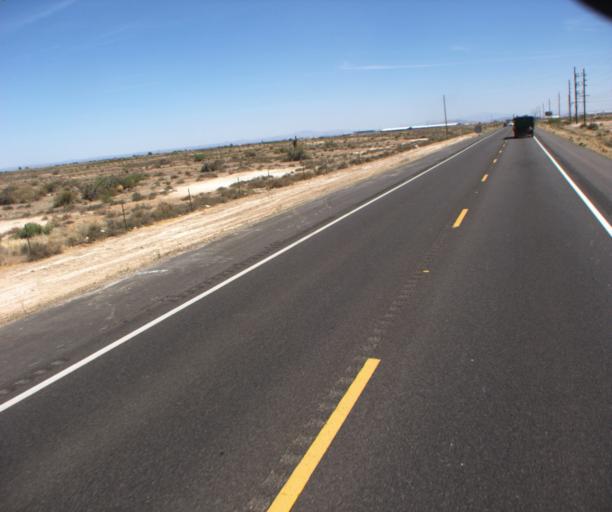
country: US
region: Arizona
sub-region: Pinal County
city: Blackwater
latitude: 33.0087
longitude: -111.6192
